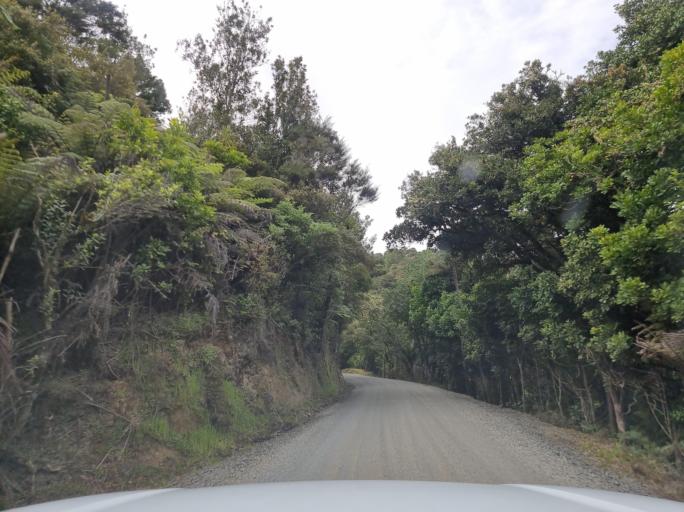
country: NZ
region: Northland
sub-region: Whangarei
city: Ruakaka
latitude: -36.0424
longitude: 174.4101
